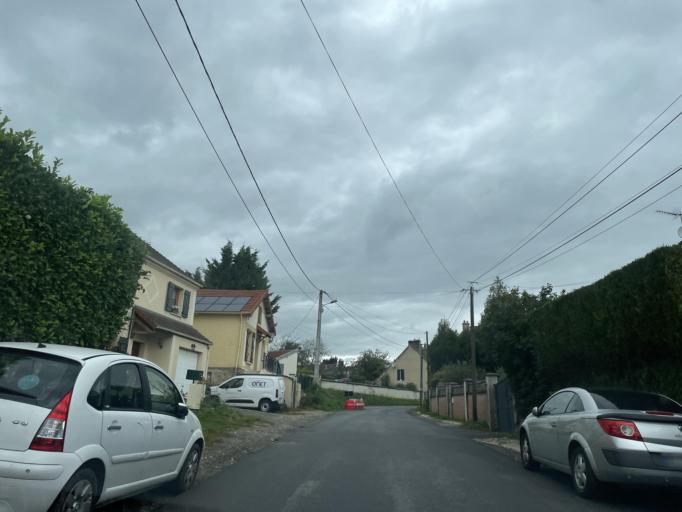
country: FR
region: Ile-de-France
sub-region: Departement de Seine-et-Marne
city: Coulommiers
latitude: 48.8210
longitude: 3.1037
